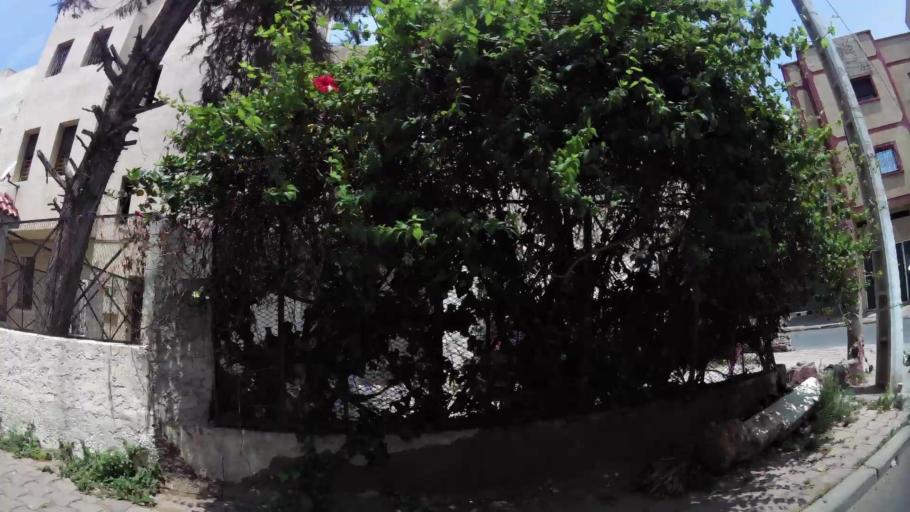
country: MA
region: Rabat-Sale-Zemmour-Zaer
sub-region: Skhirate-Temara
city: Temara
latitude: 33.9783
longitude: -6.8862
